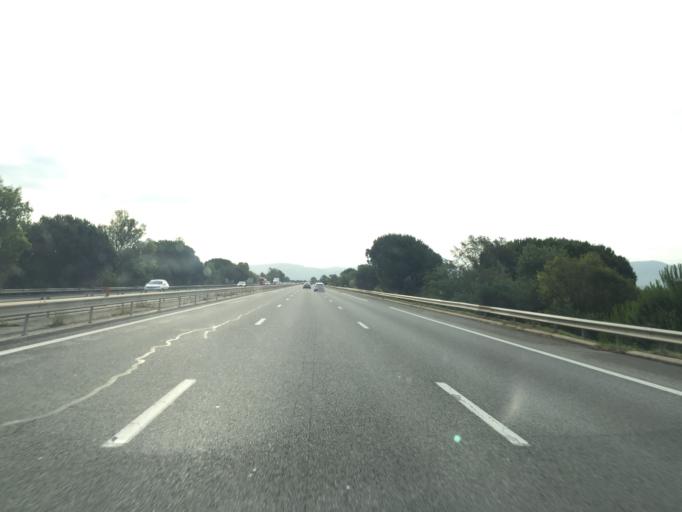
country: FR
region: Provence-Alpes-Cote d'Azur
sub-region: Departement du Var
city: Vidauban
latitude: 43.4024
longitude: 6.3936
